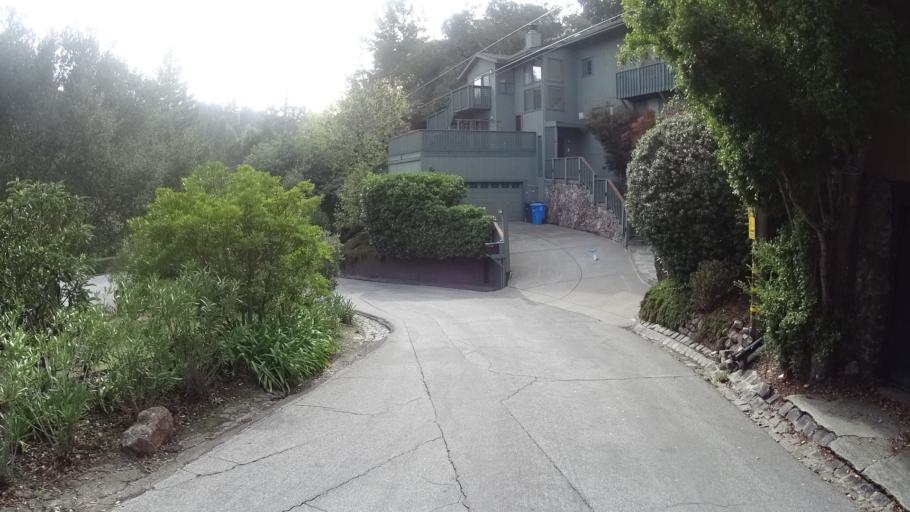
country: US
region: California
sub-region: San Mateo County
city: Hillsborough
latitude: 37.5750
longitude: -122.3881
